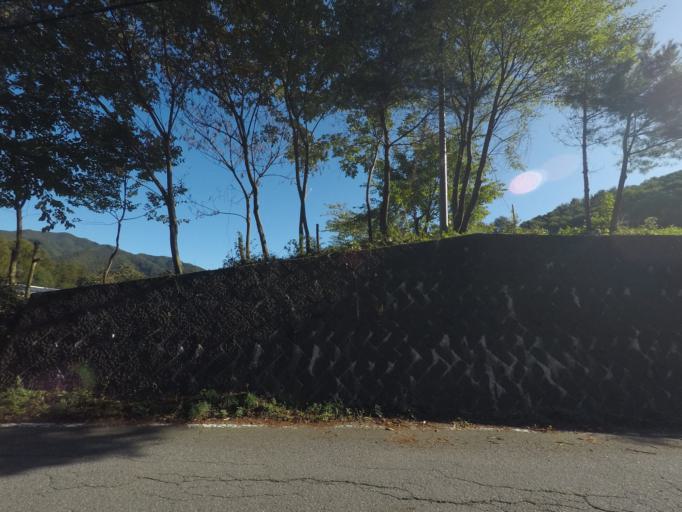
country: JP
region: Nagano
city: Ina
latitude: 35.9644
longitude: 137.7514
